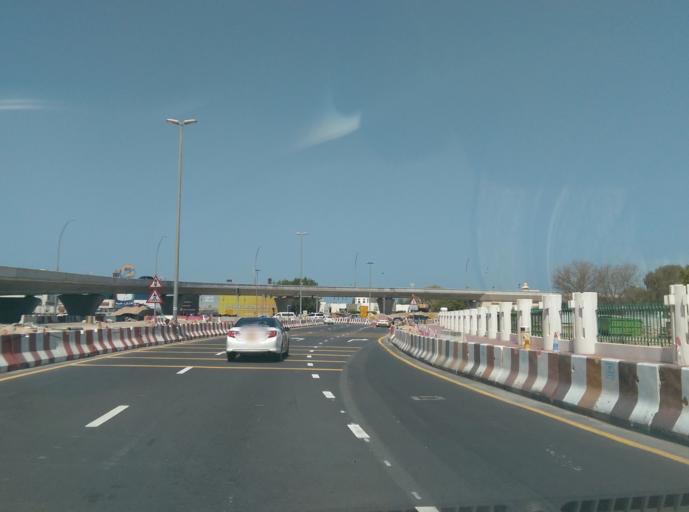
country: AE
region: Dubai
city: Dubai
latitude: 25.1861
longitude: 55.2414
